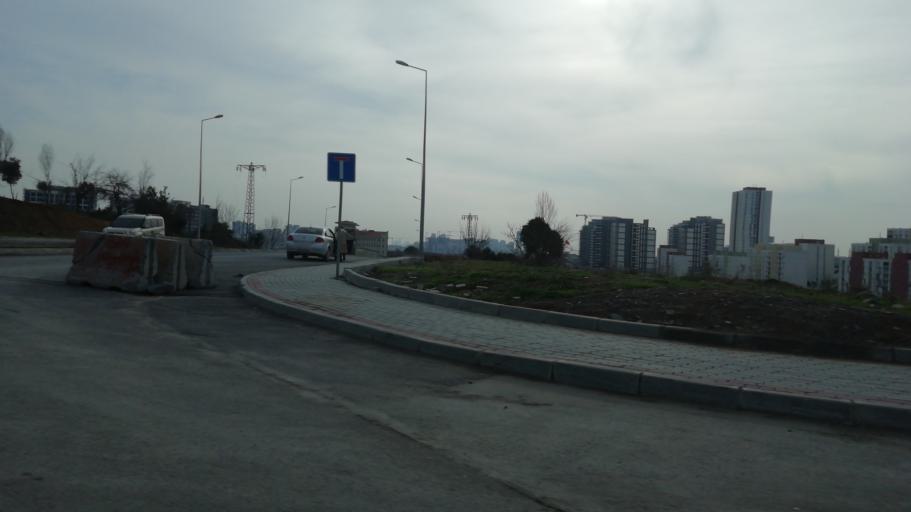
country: TR
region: Istanbul
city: Basaksehir
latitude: 41.1298
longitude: 28.7859
